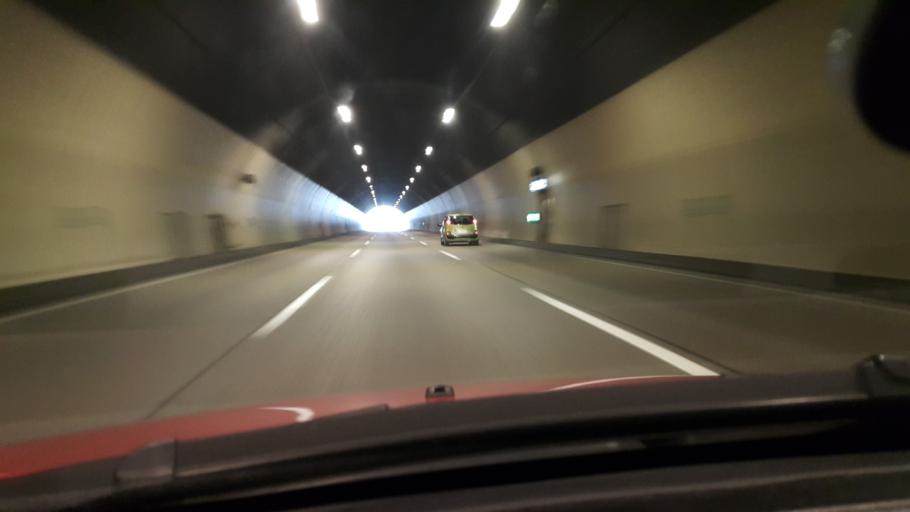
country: AT
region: Styria
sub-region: Politischer Bezirk Graz-Umgebung
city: Gratkorn
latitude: 47.1266
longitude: 15.3645
